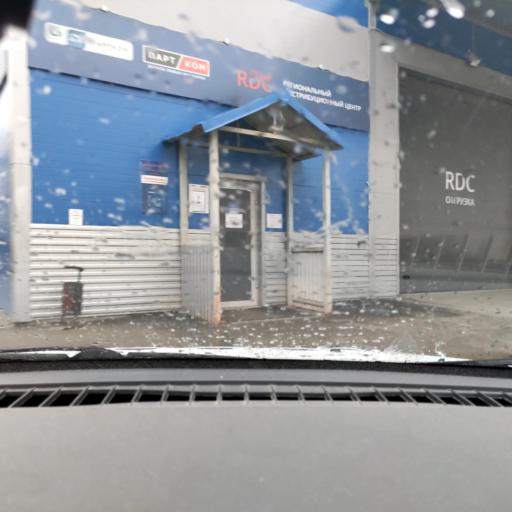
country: RU
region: Perm
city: Kondratovo
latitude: 57.9437
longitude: 56.1506
